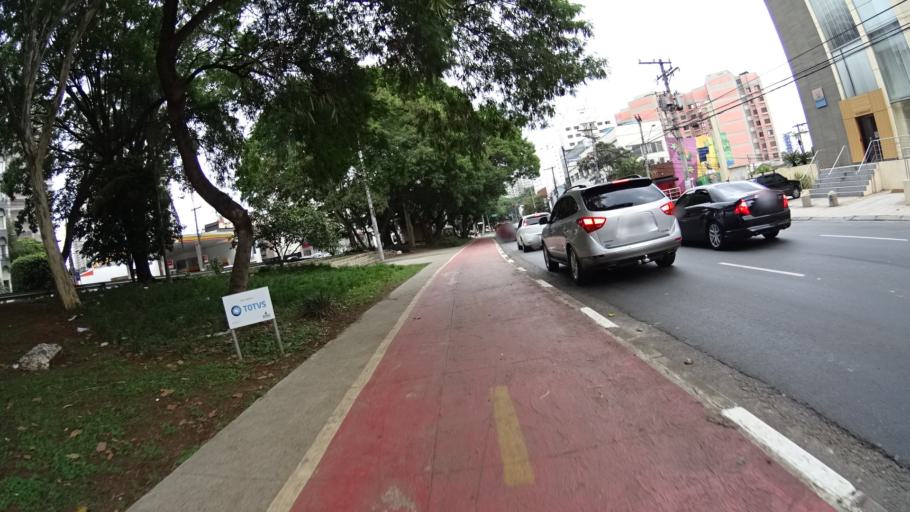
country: BR
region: Sao Paulo
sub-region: Sao Paulo
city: Sao Paulo
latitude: -23.5049
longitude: -46.6414
